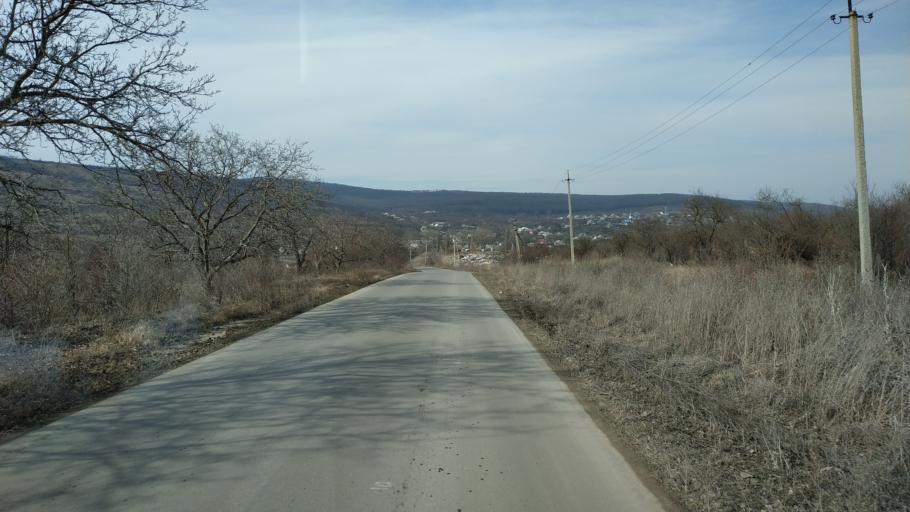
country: MD
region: Nisporeni
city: Nisporeni
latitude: 47.1468
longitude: 28.1174
